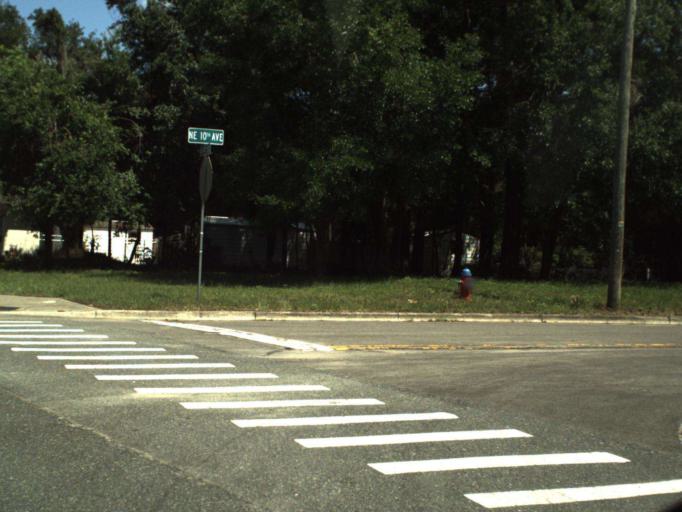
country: US
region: Florida
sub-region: Marion County
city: Ocala
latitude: 29.2005
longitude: -82.1278
